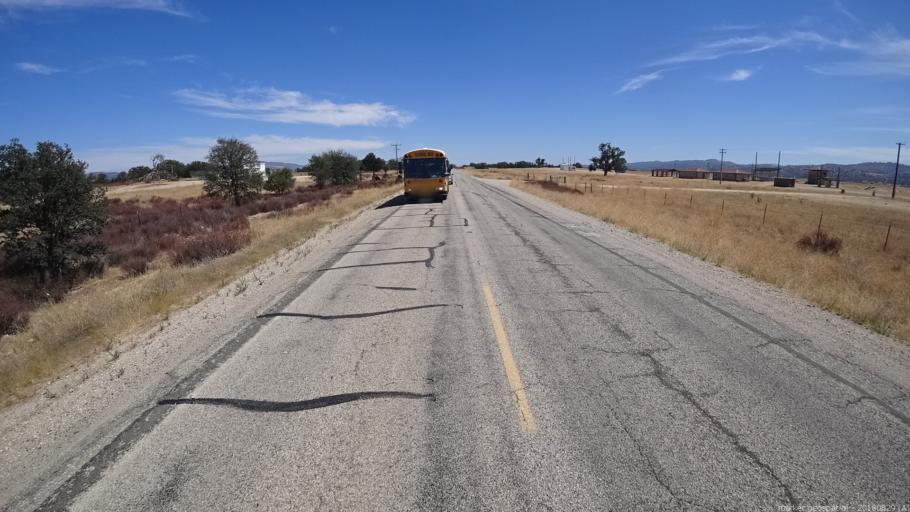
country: US
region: California
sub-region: Monterey County
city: King City
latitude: 35.9618
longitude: -121.1644
